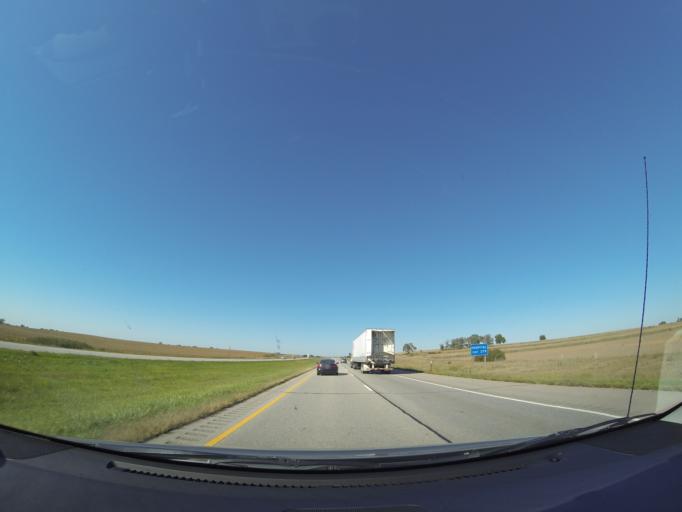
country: US
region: Nebraska
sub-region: Seward County
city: Milford
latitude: 40.8223
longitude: -97.0895
